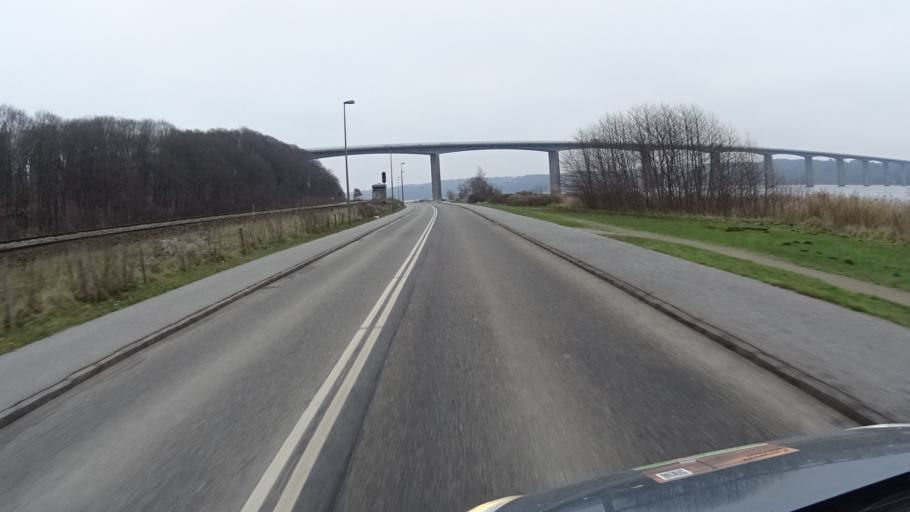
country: DK
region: South Denmark
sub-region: Vejle Kommune
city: Vejle
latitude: 55.7074
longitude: 9.5692
